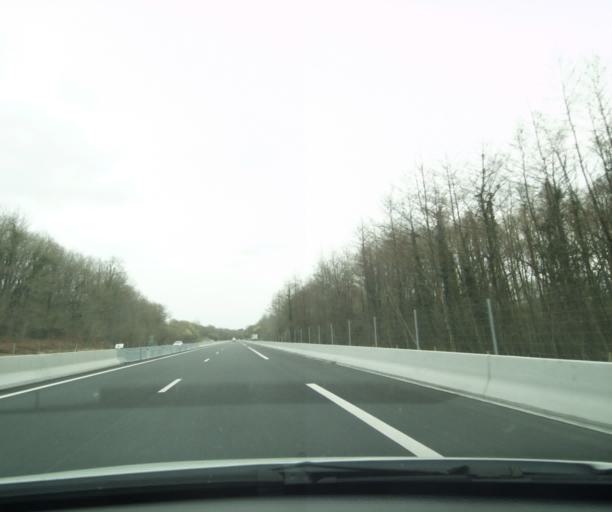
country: FR
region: Aquitaine
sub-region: Departement des Pyrenees-Atlantiques
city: Mouguerre
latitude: 43.4557
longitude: -1.4097
